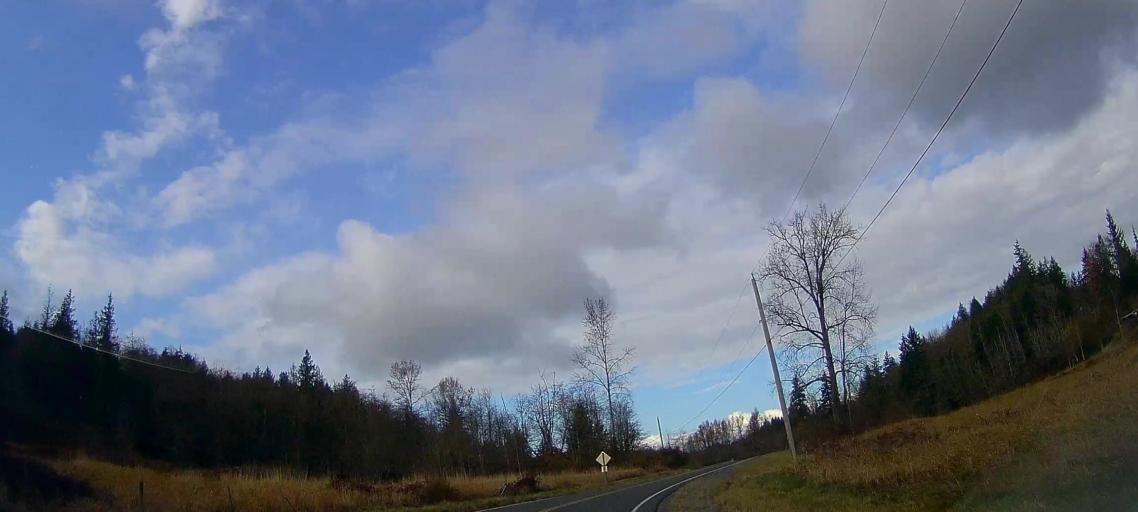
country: US
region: Washington
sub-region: Skagit County
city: Big Lake
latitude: 48.4059
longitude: -122.2157
